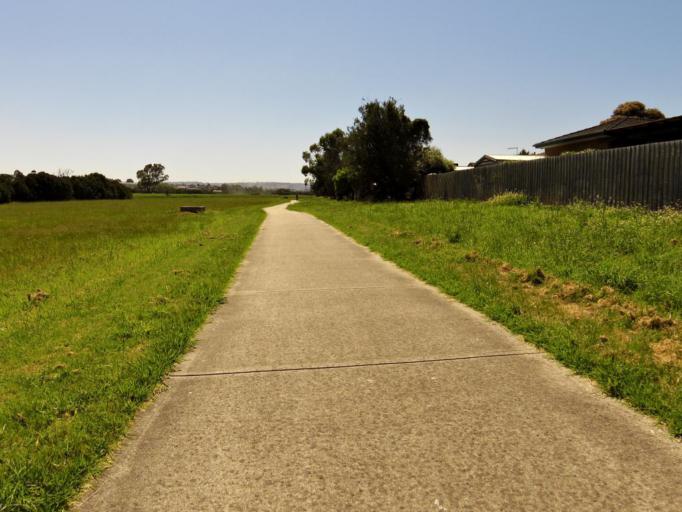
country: AU
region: Victoria
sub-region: Casey
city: Hallam
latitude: -38.0215
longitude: 145.2611
